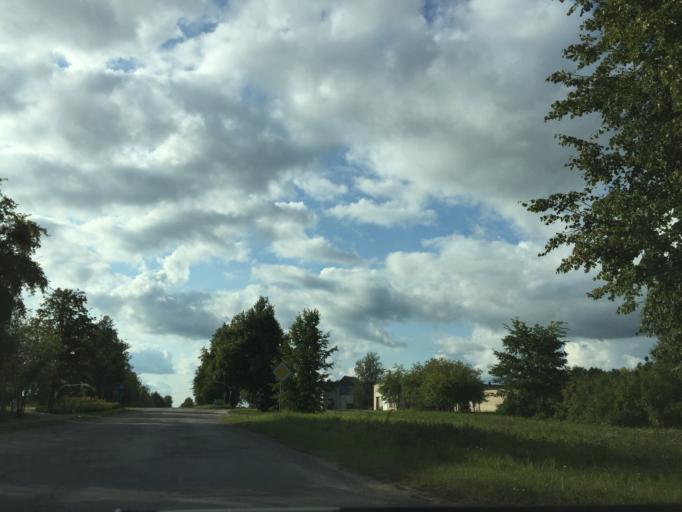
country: LV
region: Kegums
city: Kegums
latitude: 56.8089
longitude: 24.7327
